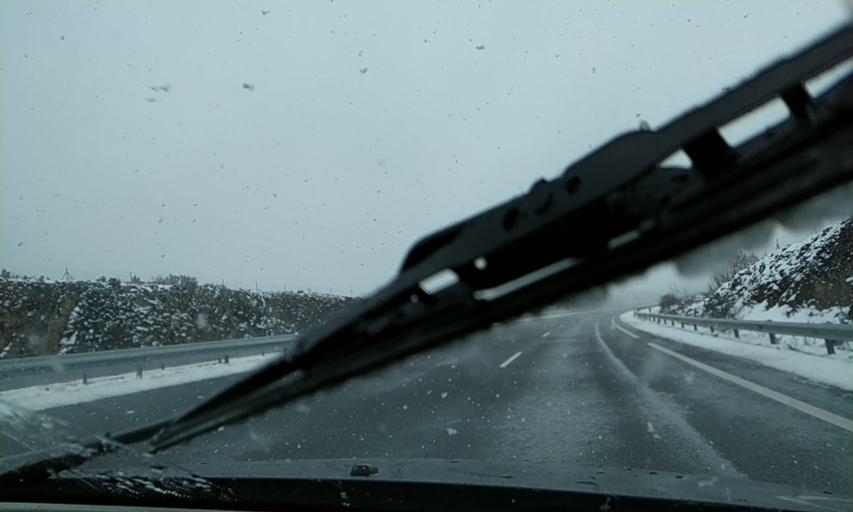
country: ES
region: Galicia
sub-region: Provincia de Ourense
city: Rios
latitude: 42.0129
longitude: -7.2007
